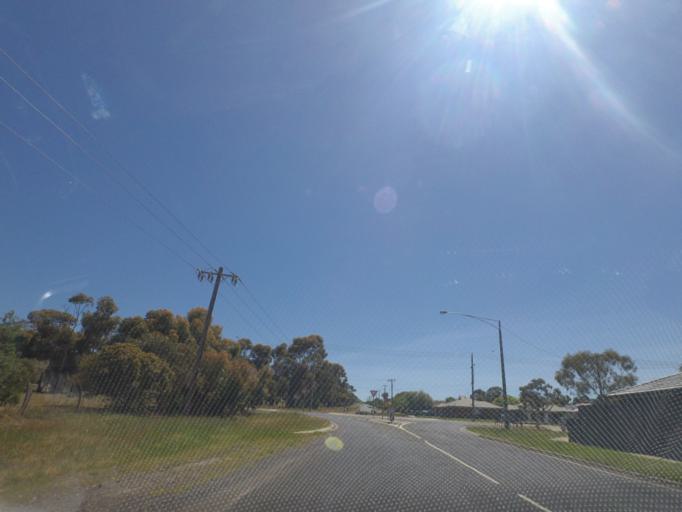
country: AU
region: Victoria
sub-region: Hume
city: Sunbury
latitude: -37.5772
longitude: 144.6936
